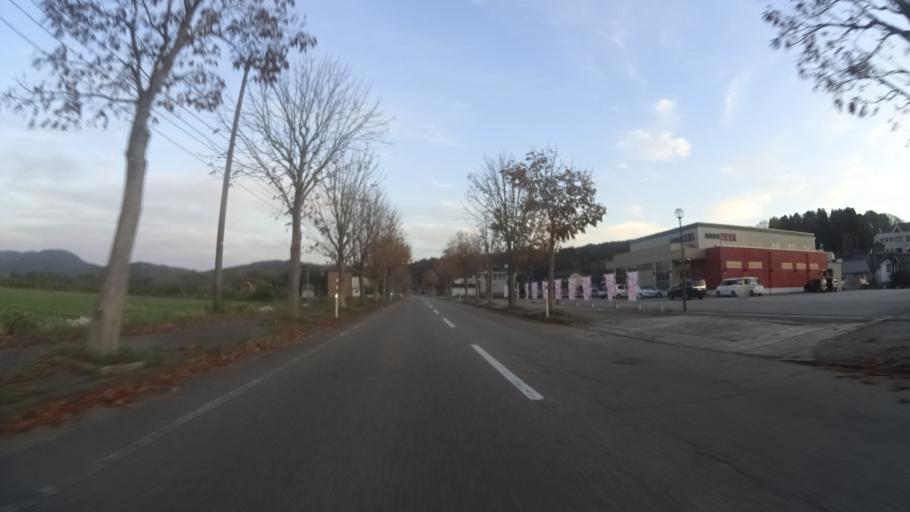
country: JP
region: Ishikawa
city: Nanao
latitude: 37.2917
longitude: 136.7704
